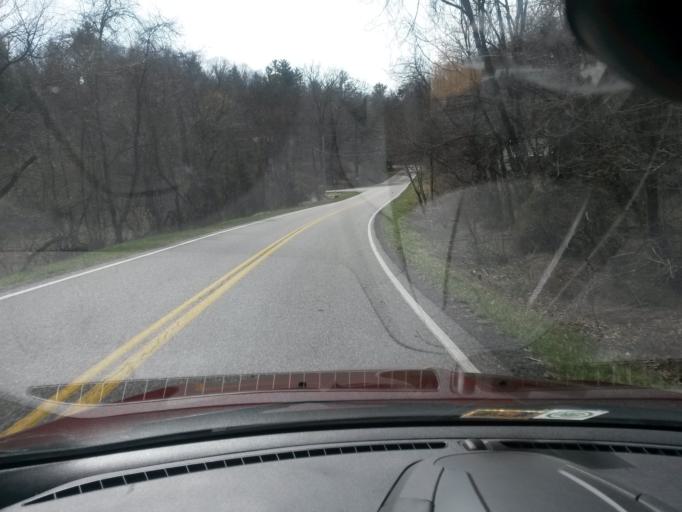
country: US
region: West Virginia
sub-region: Greenbrier County
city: White Sulphur Springs
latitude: 37.6787
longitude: -80.2326
